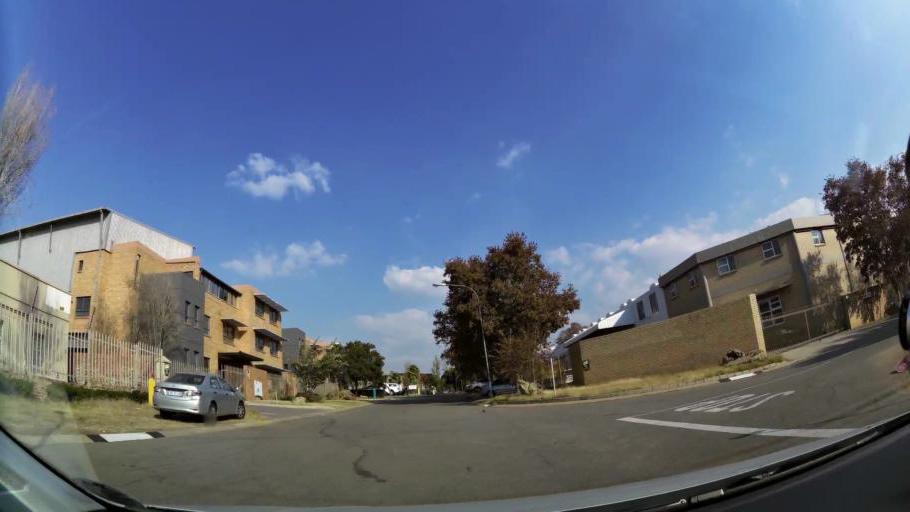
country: ZA
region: Gauteng
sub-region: City of Johannesburg Metropolitan Municipality
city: Modderfontein
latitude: -26.1056
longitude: 28.1758
